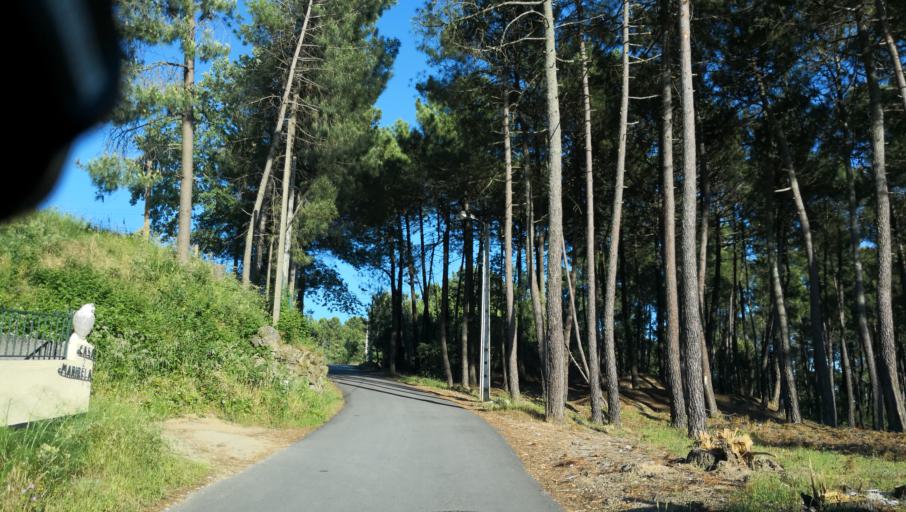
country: PT
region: Vila Real
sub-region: Vila Real
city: Vila Real
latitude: 41.3160
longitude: -7.7001
